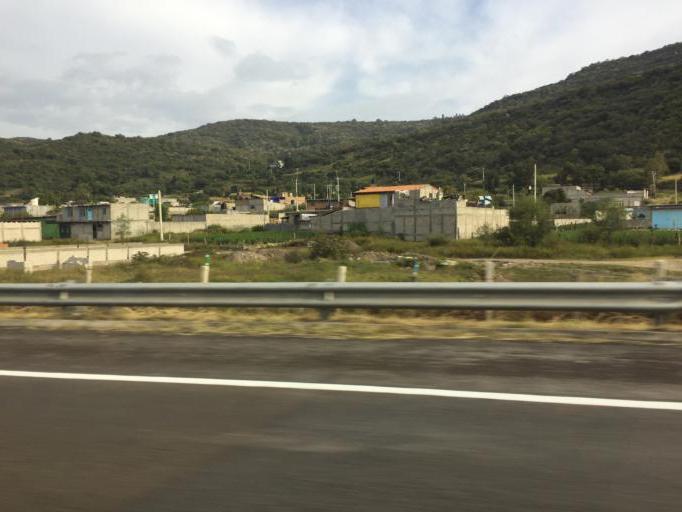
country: MX
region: Michoacan
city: Copandaro de Galeana
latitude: 19.8822
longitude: -101.1986
